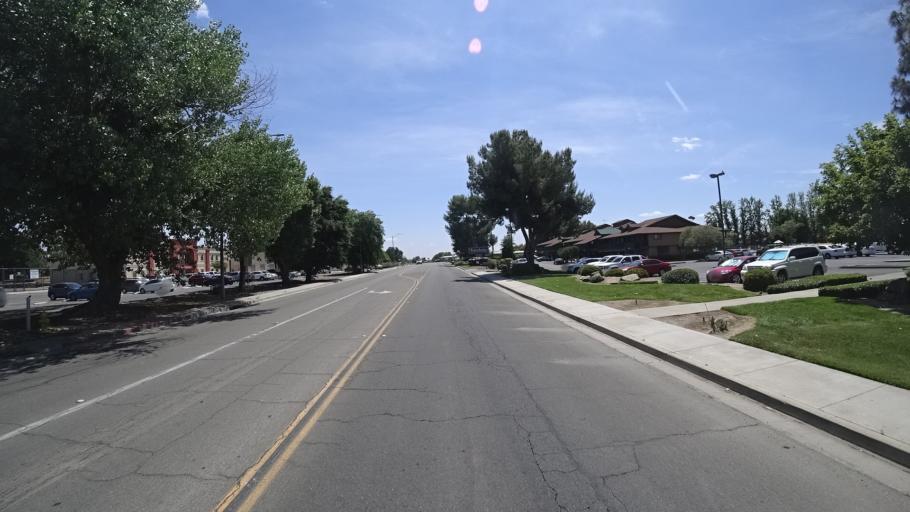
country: US
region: California
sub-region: Kings County
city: Lemoore
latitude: 36.2999
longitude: -119.7686
